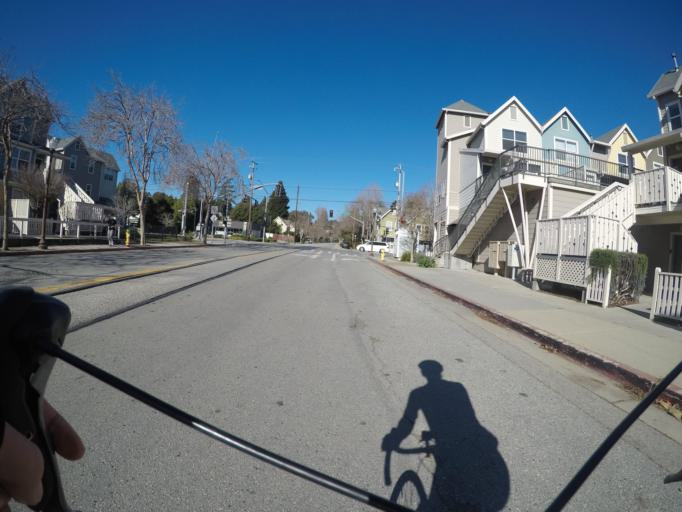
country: US
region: California
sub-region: Santa Cruz County
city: Santa Cruz
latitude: 36.9683
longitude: -122.0292
